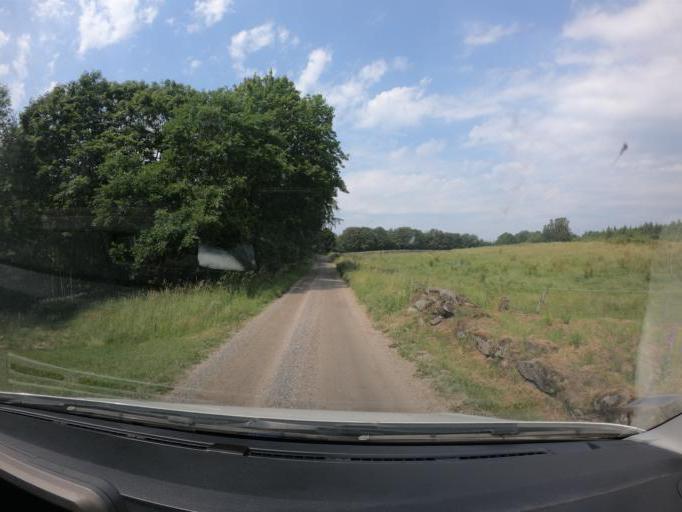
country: SE
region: Skane
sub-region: Hassleholms Kommun
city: Bjarnum
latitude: 56.2876
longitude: 13.6241
